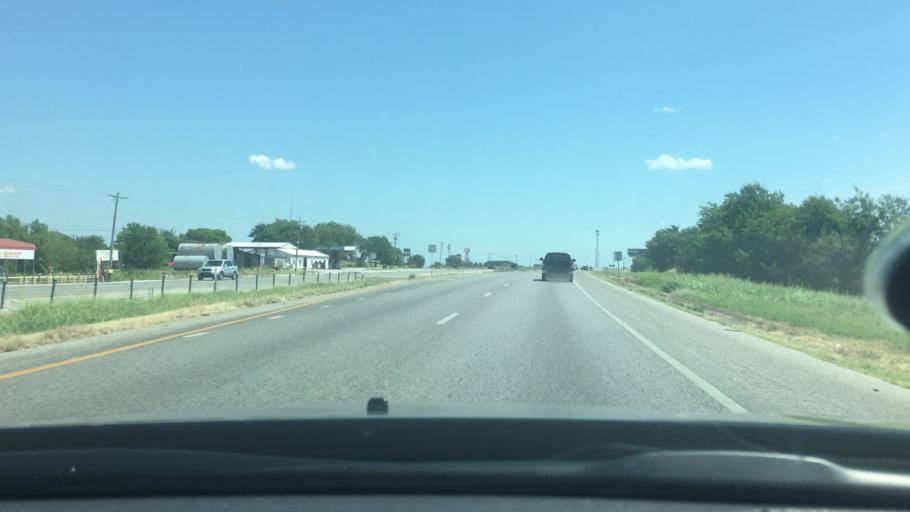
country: US
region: Oklahoma
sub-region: Bryan County
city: Calera
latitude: 33.9054
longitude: -96.4662
